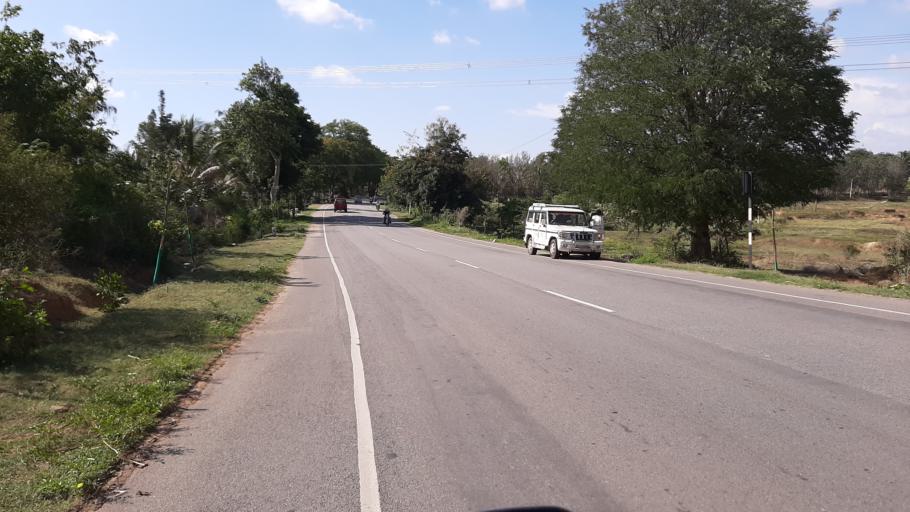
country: IN
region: Tamil Nadu
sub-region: Krishnagiri
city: Denkanikota
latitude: 12.5437
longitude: 77.7882
